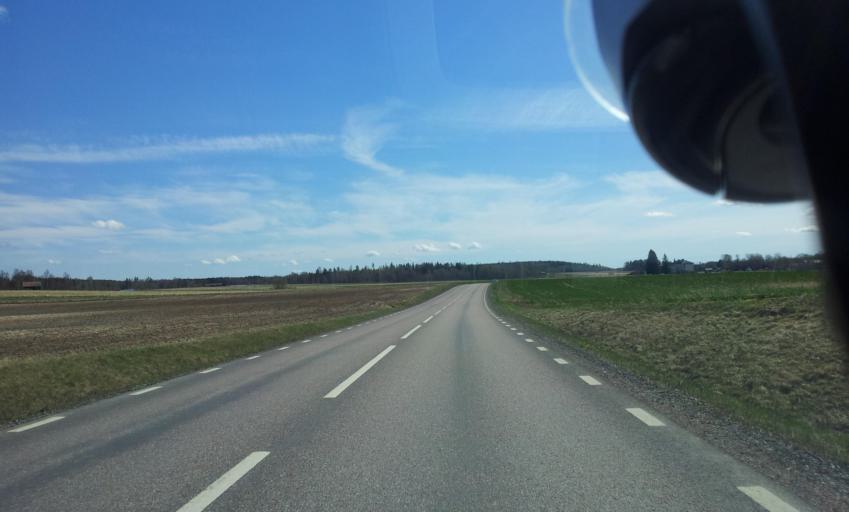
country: SE
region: Dalarna
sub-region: Borlange Kommun
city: Borlaenge
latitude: 60.4809
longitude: 15.4878
